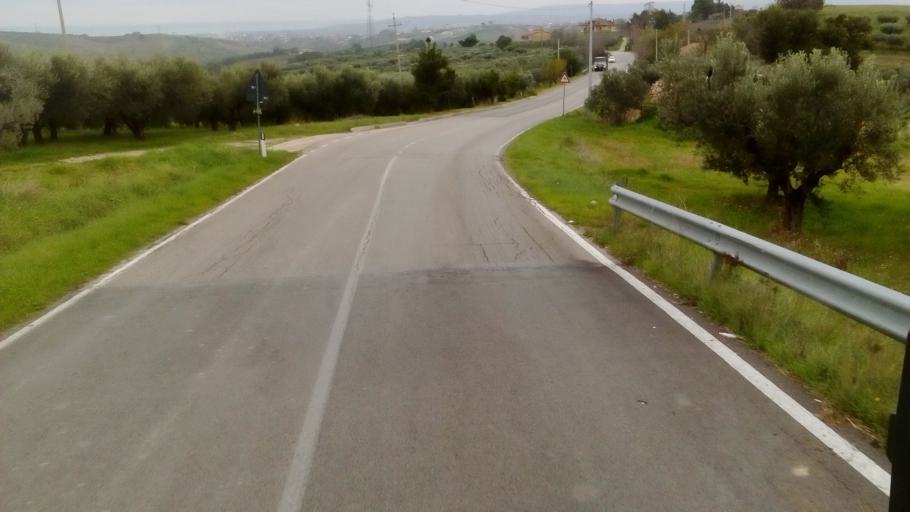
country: IT
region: Abruzzo
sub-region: Provincia di Chieti
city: Cupello
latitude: 42.0593
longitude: 14.6952
